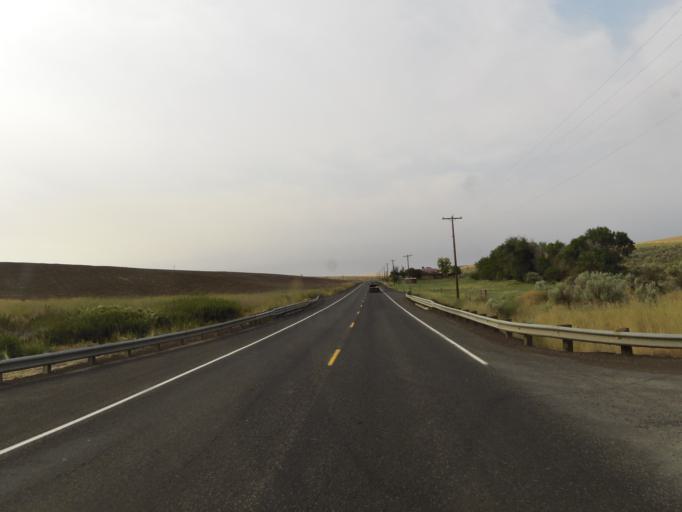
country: US
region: Oregon
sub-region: Sherman County
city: Moro
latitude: 45.4702
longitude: -120.7461
